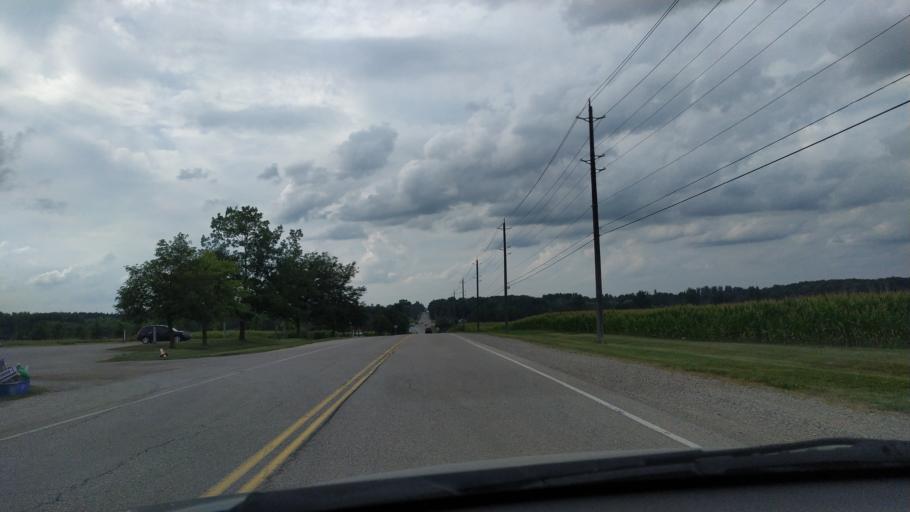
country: CA
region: Ontario
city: Kitchener
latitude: 43.3661
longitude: -80.5539
